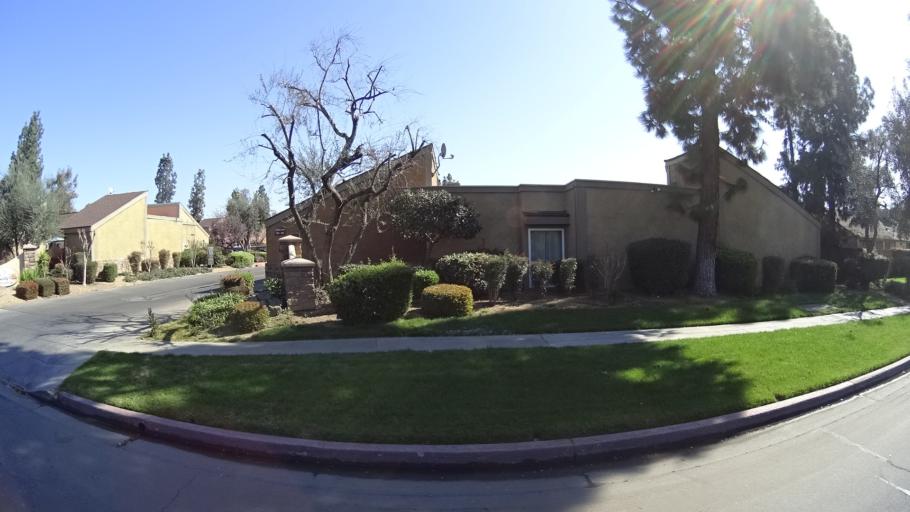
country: US
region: California
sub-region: Fresno County
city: Fresno
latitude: 36.8396
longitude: -119.8174
